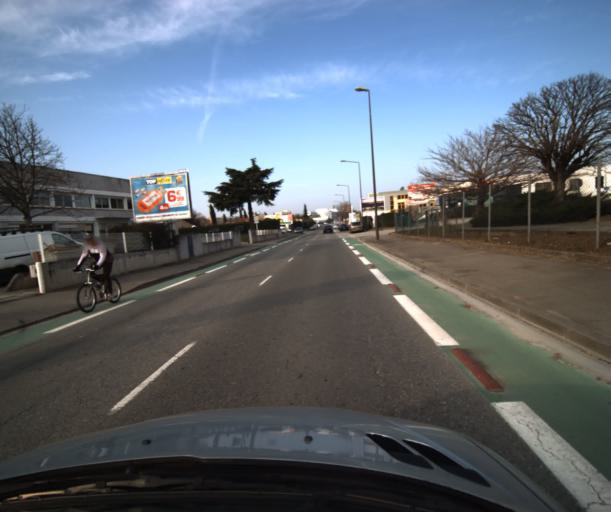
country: FR
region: Midi-Pyrenees
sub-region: Departement de la Haute-Garonne
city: Ramonville-Saint-Agne
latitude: 43.5697
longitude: 1.4914
